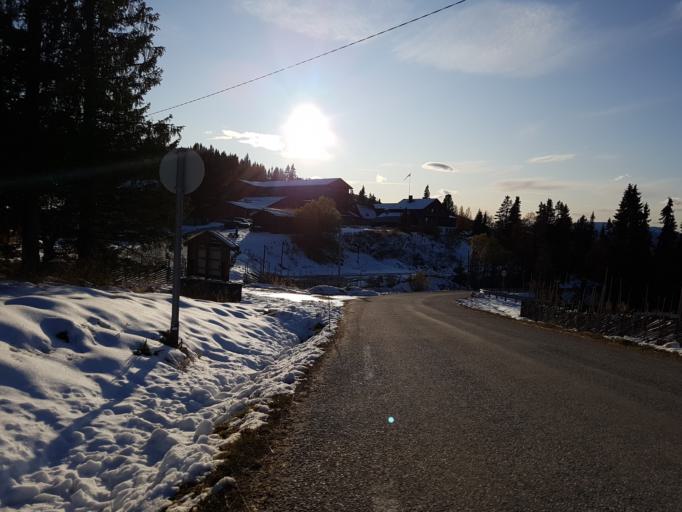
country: NO
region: Oppland
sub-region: Sel
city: Otta
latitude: 61.8093
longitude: 9.6761
